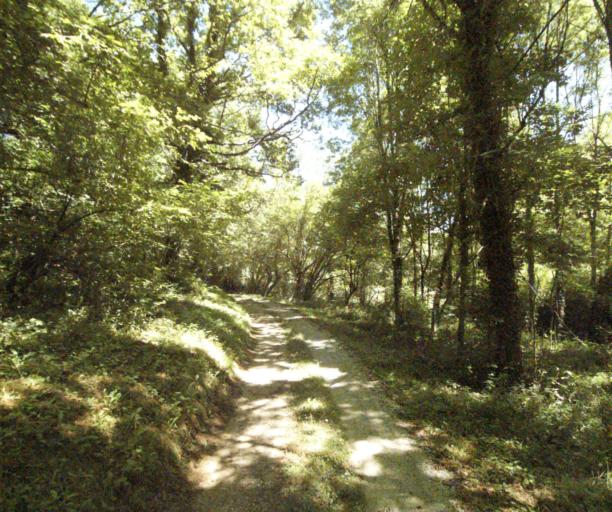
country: FR
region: Midi-Pyrenees
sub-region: Departement du Tarn
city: Dourgne
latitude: 43.4239
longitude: 2.1676
